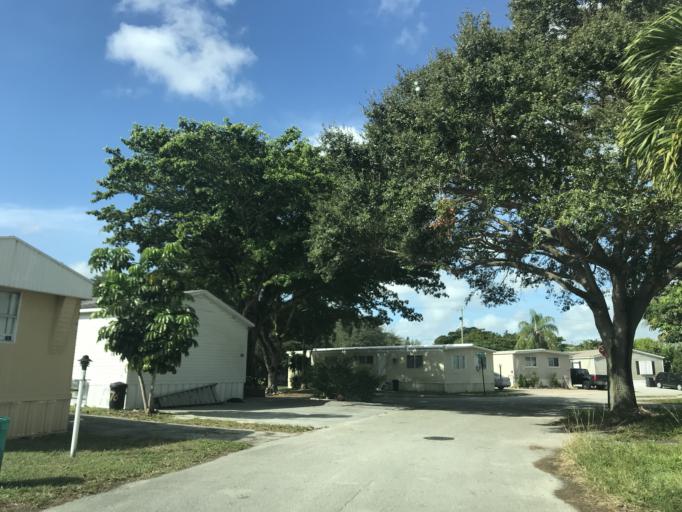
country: US
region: Florida
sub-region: Palm Beach County
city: Boca Pointe
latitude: 26.3119
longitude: -80.1760
